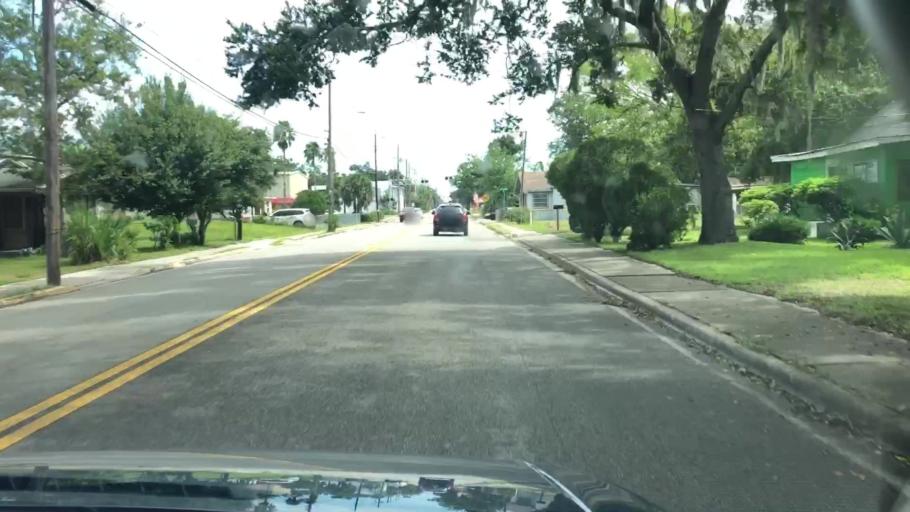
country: US
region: Florida
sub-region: Volusia County
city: Daytona Beach
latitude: 29.1959
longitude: -81.0194
